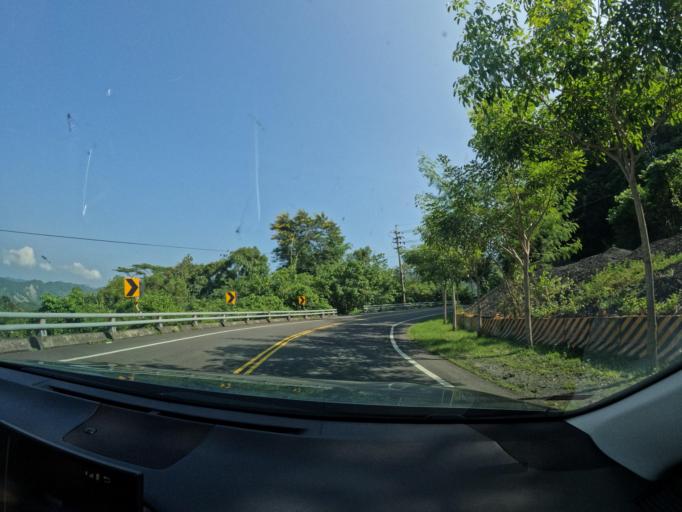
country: TW
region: Taiwan
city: Yujing
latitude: 23.0778
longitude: 120.6174
